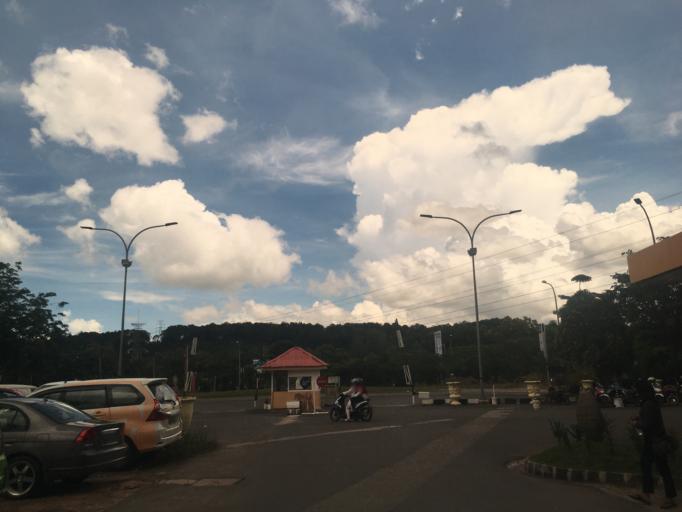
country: SG
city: Singapore
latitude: 1.1173
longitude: 104.0233
